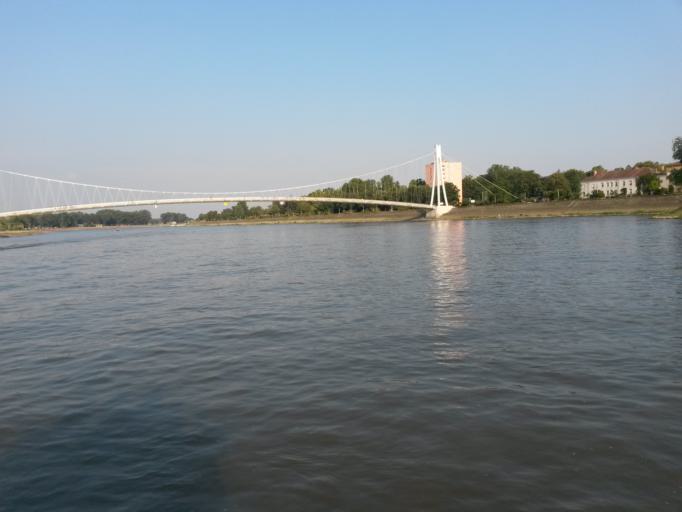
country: HR
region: Osjecko-Baranjska
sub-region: Grad Osijek
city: Osijek
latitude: 45.5637
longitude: 18.6823
